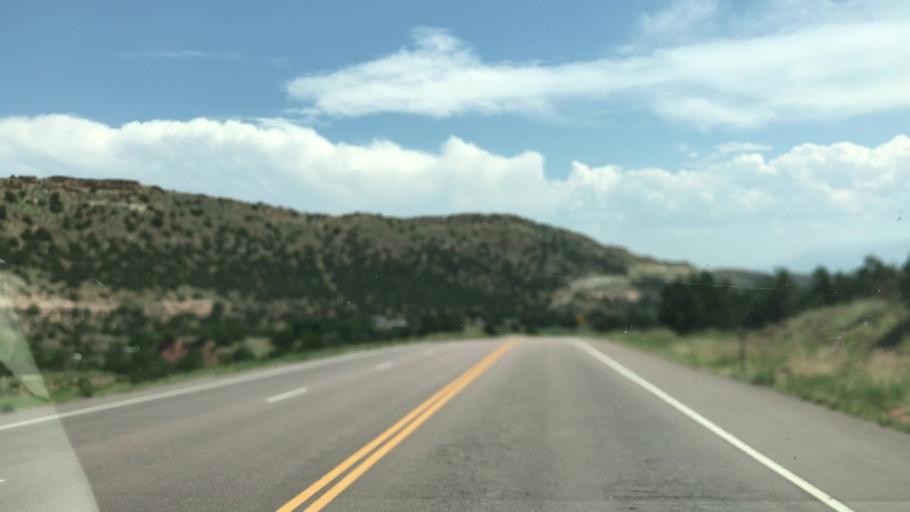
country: US
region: Colorado
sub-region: Fremont County
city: Canon City
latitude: 38.4777
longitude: -105.2615
